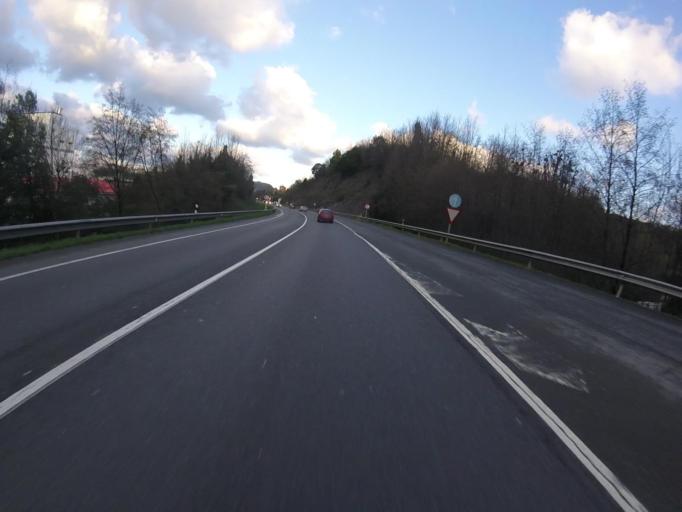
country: ES
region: Basque Country
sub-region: Provincia de Guipuzcoa
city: Lezo
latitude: 43.3135
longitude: -1.8928
